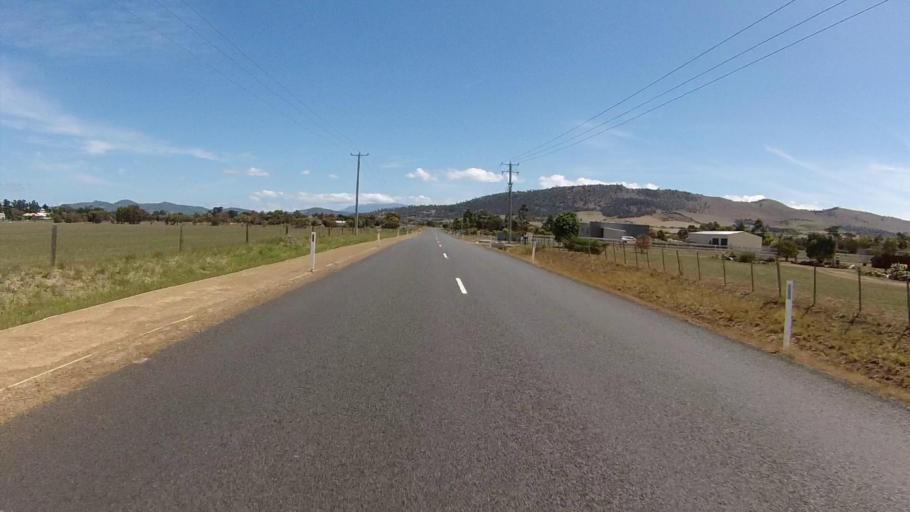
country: AU
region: Tasmania
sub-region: Sorell
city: Sorell
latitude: -42.7774
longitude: 147.5276
